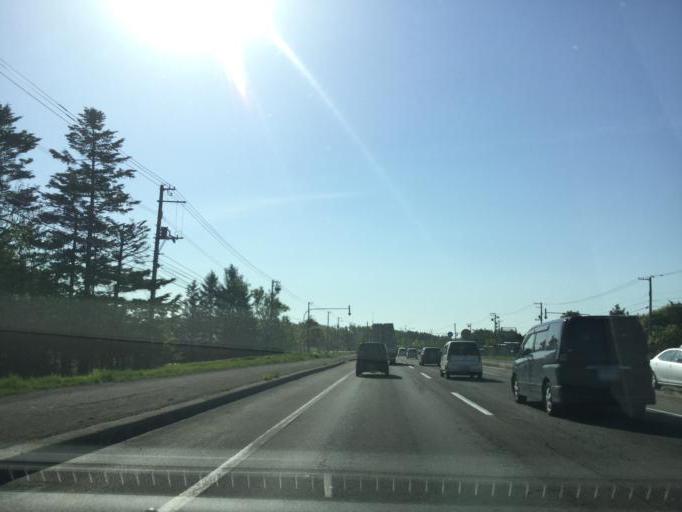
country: JP
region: Hokkaido
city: Kitahiroshima
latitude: 43.0055
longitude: 141.5270
